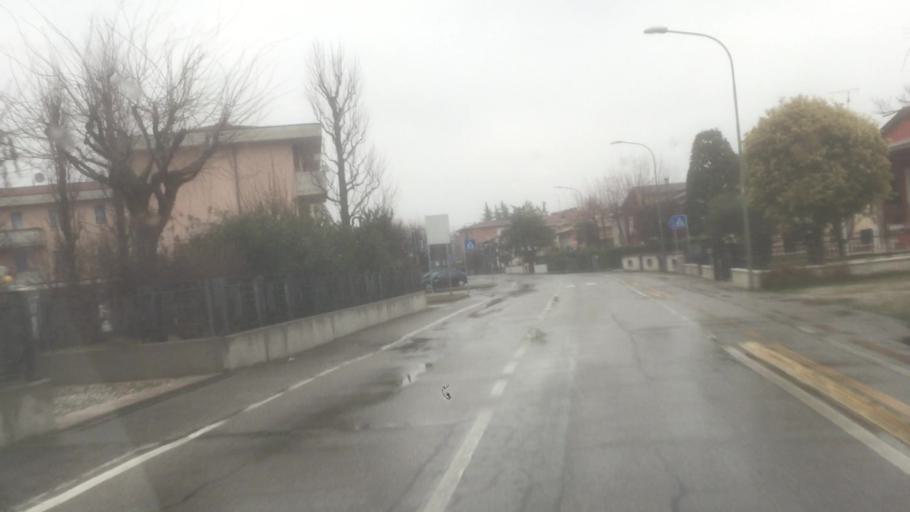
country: IT
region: Lombardy
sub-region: Provincia di Mantova
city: Castel Goffredo
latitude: 45.2943
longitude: 10.4697
